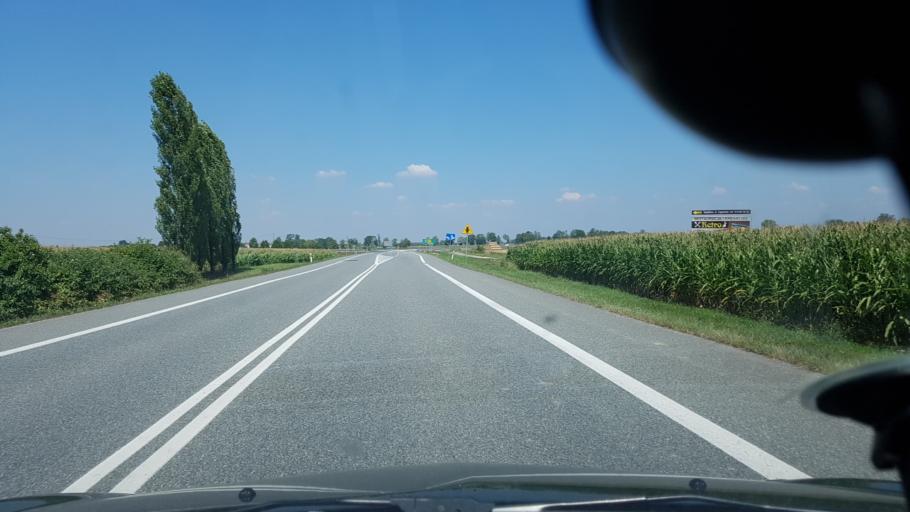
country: PL
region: Silesian Voivodeship
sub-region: Powiat wodzislawski
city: Olza
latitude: 49.9407
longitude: 18.3289
